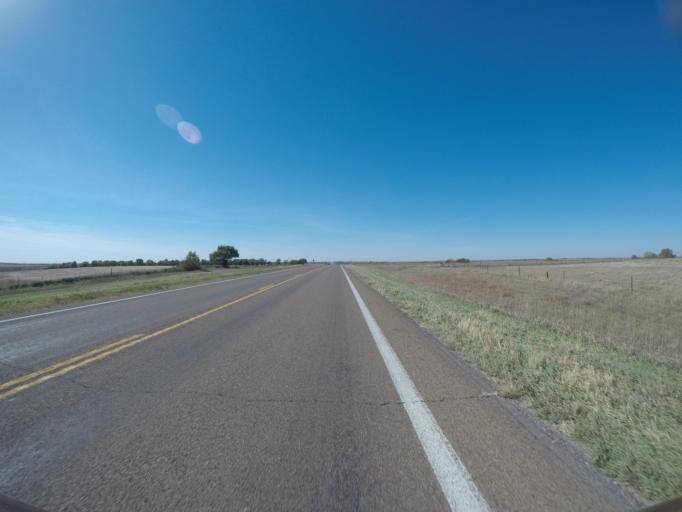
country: US
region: Kansas
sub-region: Smith County
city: Smith Center
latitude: 39.7856
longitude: -98.7248
